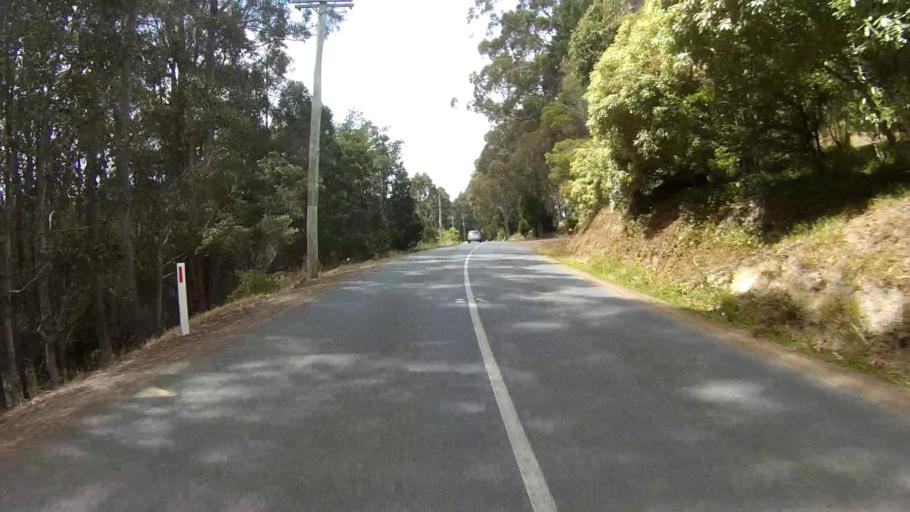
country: AU
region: Tasmania
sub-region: Kingborough
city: Kettering
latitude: -43.1055
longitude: 147.2373
